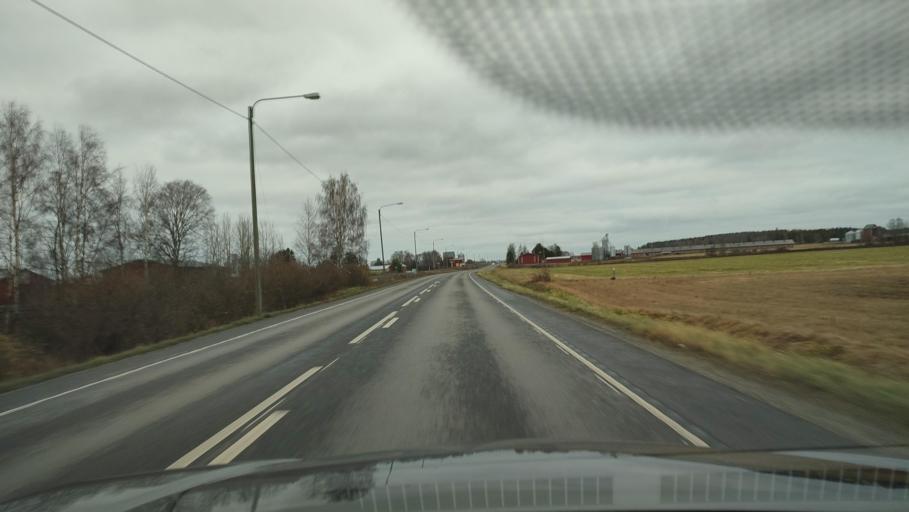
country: FI
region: Southern Ostrobothnia
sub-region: Seinaejoki
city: Ilmajoki
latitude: 62.7042
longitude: 22.5222
